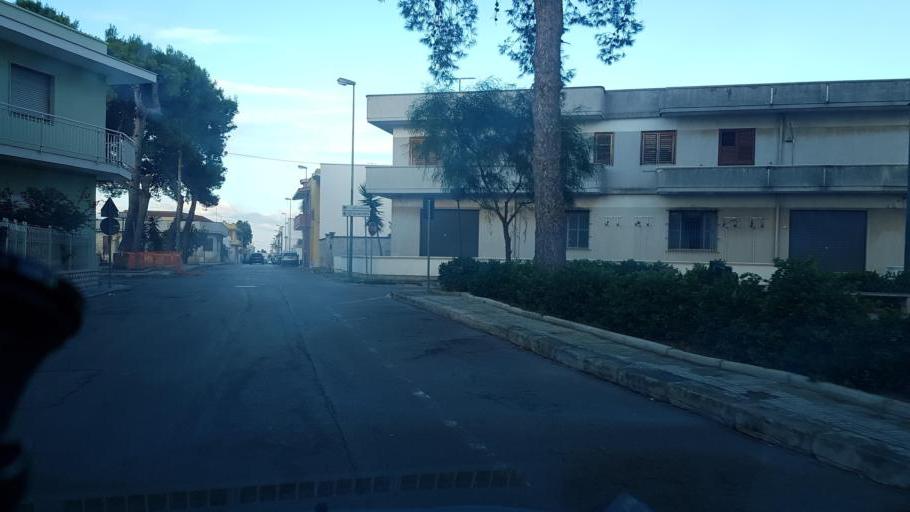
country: IT
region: Apulia
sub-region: Provincia di Brindisi
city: Cellino San Marco
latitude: 40.4668
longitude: 17.9657
